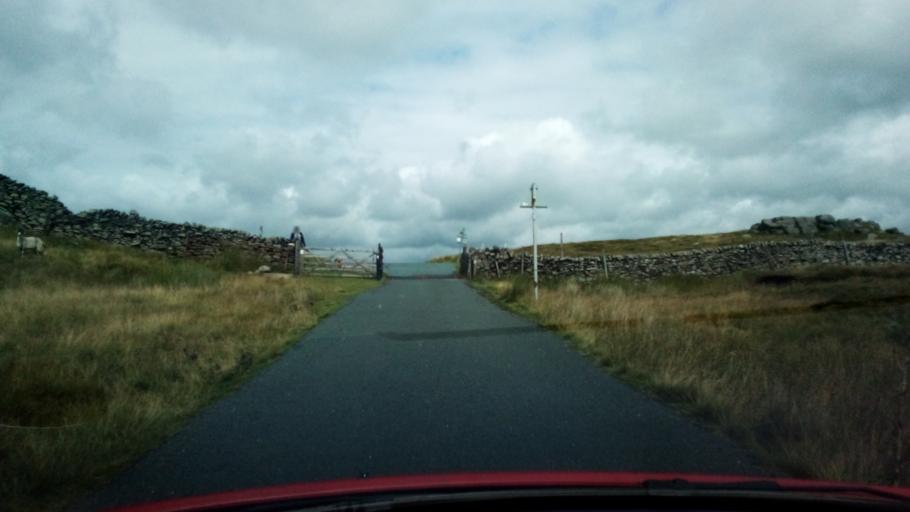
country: GB
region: England
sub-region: North Yorkshire
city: High Bentham
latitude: 54.0410
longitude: -2.4189
